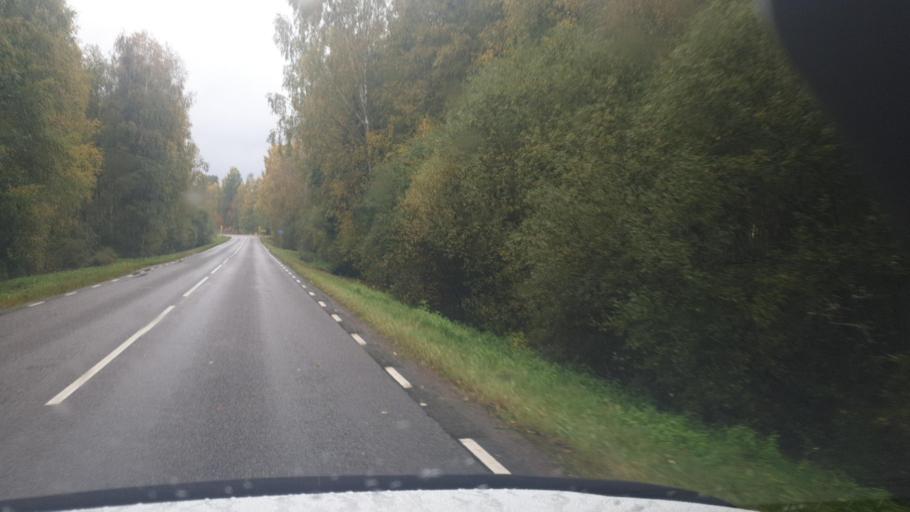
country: SE
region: Vaermland
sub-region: Sunne Kommun
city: Sunne
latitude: 59.7994
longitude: 13.0541
